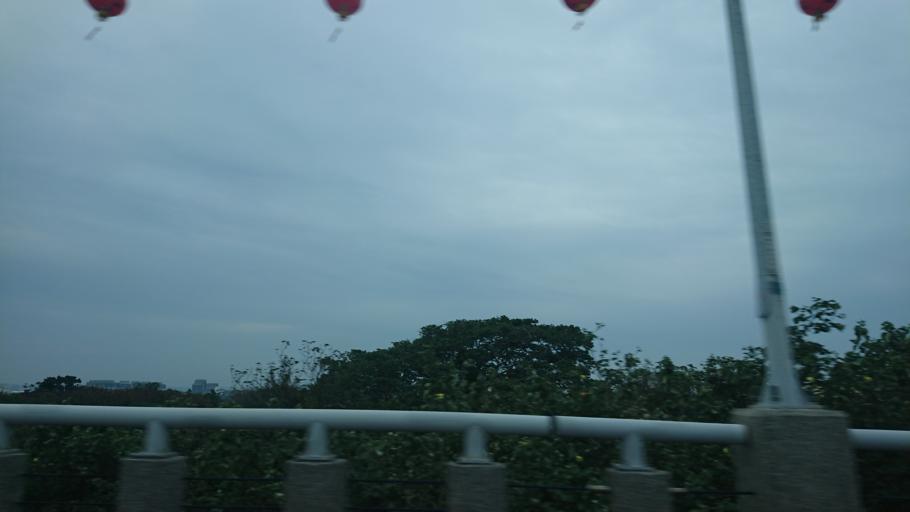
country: TW
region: Taiwan
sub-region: Hsinchu
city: Hsinchu
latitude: 24.8440
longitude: 120.9437
